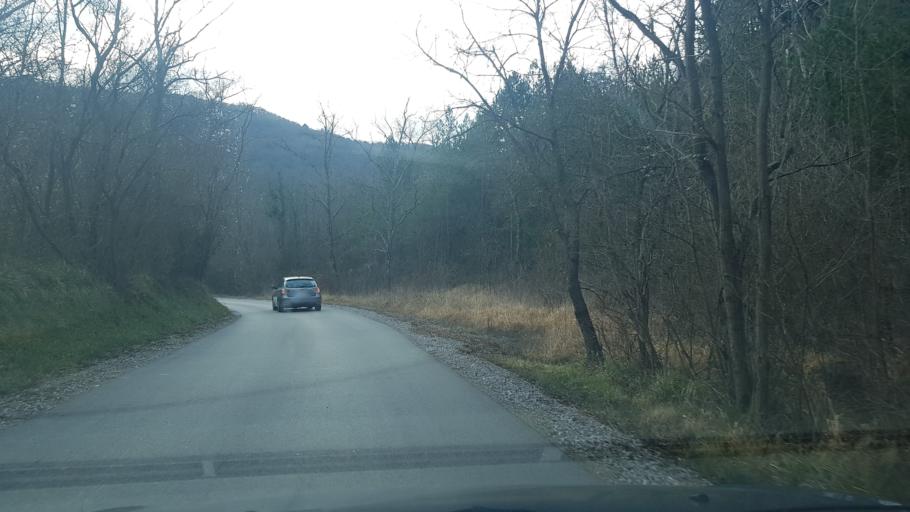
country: SI
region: Koper-Capodistria
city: Prade
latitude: 45.4865
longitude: 13.7746
